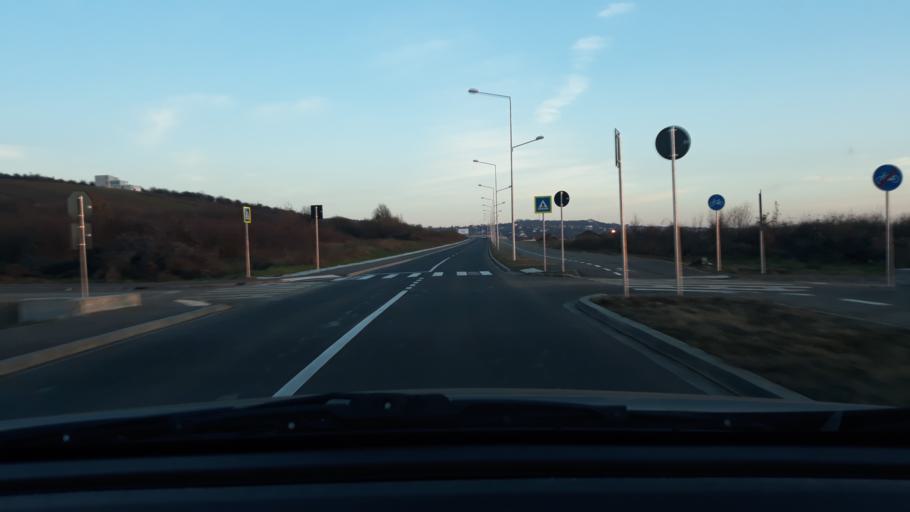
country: RO
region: Bihor
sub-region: Comuna Biharea
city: Oradea
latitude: 47.0999
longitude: 21.9162
